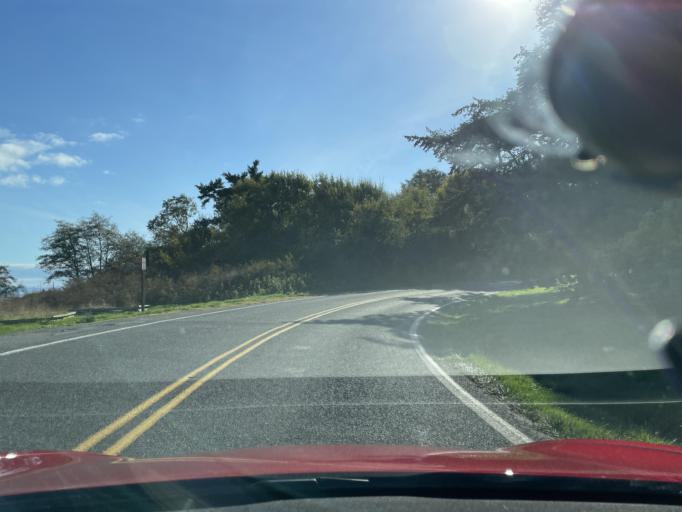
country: US
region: Washington
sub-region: San Juan County
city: Friday Harbor
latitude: 48.4541
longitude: -122.9633
